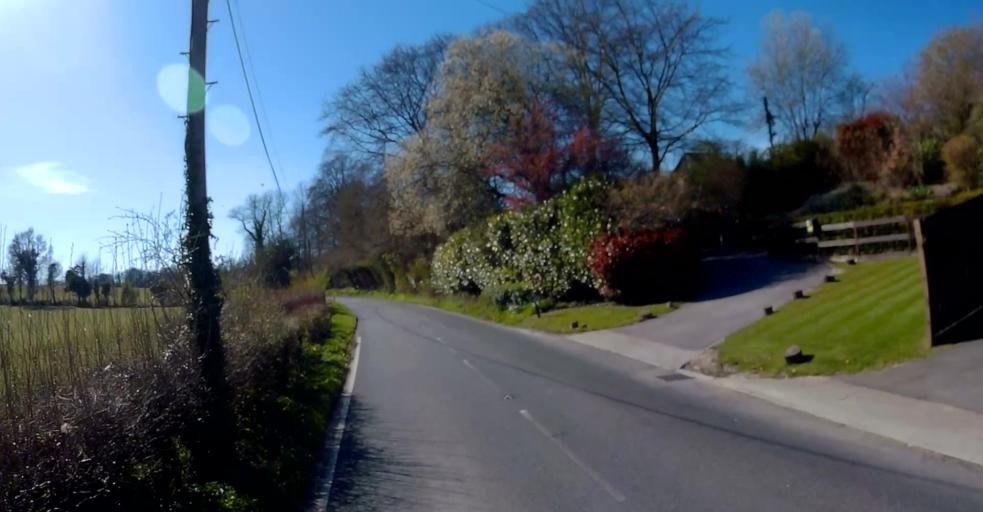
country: GB
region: England
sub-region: Surrey
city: Farnham
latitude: 51.2158
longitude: -0.8235
